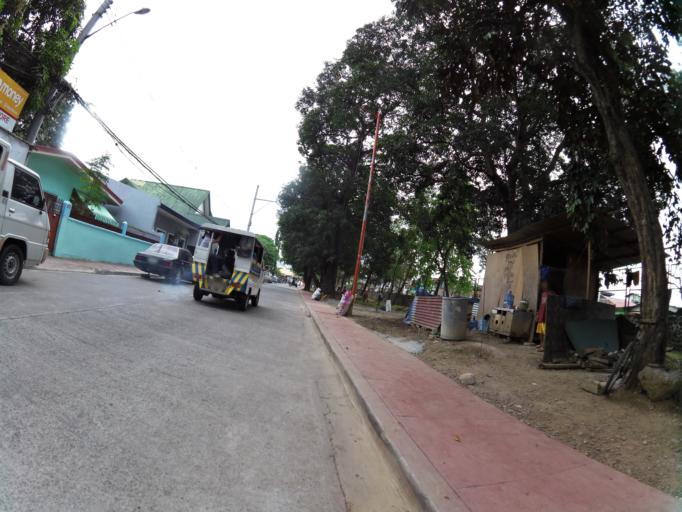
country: PH
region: Calabarzon
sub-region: Province of Rizal
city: Antipolo
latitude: 14.6382
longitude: 121.1145
